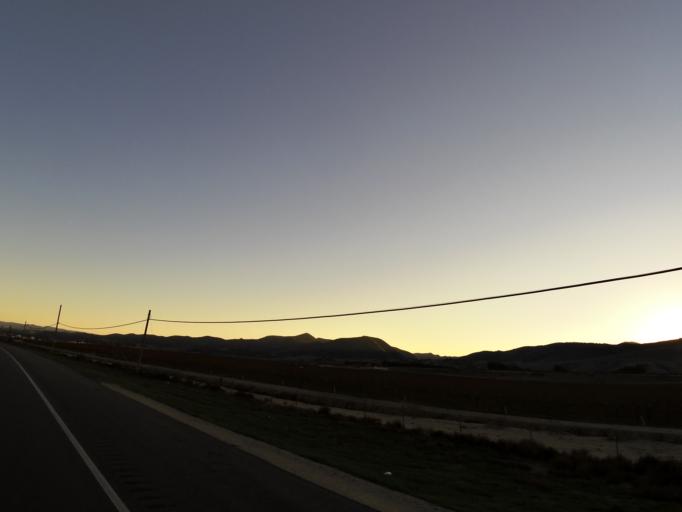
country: US
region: California
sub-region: Monterey County
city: King City
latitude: 36.2557
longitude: -121.1781
